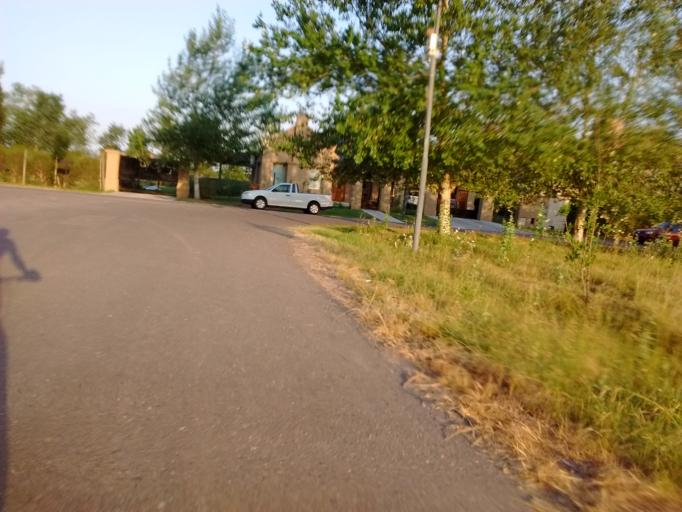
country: AR
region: Santa Fe
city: Funes
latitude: -32.9157
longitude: -60.7730
